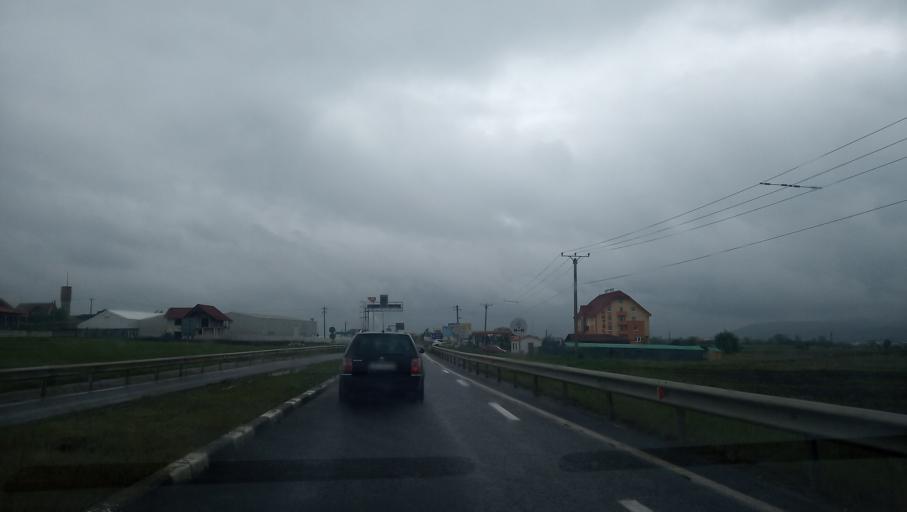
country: RO
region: Alba
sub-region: Municipiul Sebes
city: Sebes
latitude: 45.9457
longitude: 23.5888
